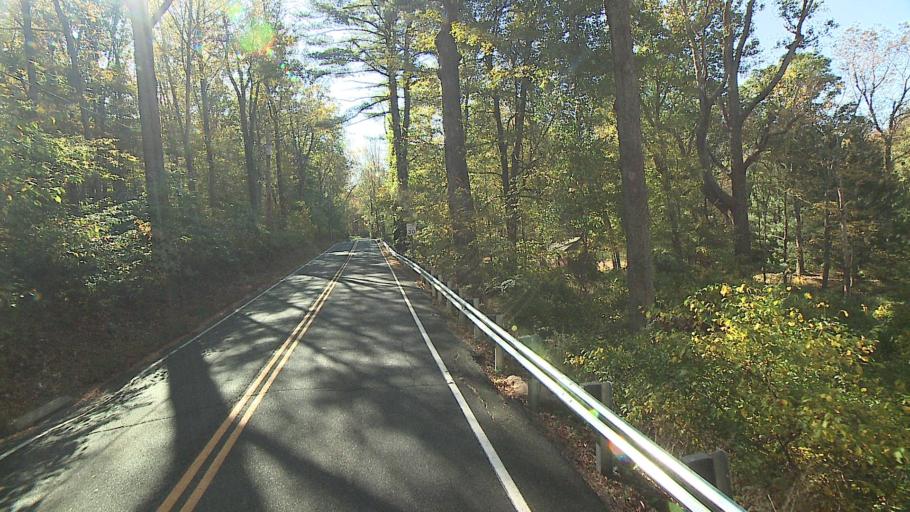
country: US
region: Connecticut
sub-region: Fairfield County
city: Westport
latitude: 41.2167
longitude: -73.3251
